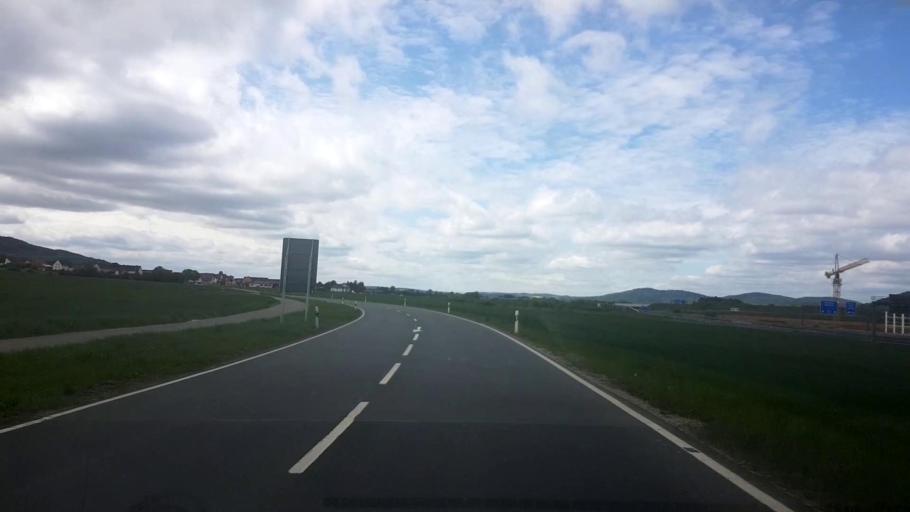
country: DE
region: Bavaria
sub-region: Upper Franconia
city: Lichtenfels
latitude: 50.1298
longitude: 11.0421
